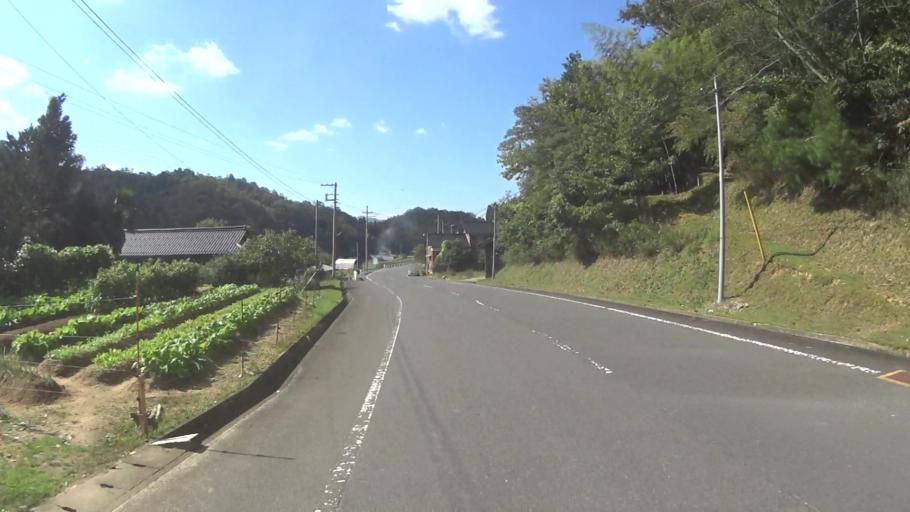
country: JP
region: Hyogo
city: Toyooka
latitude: 35.5960
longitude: 134.9801
